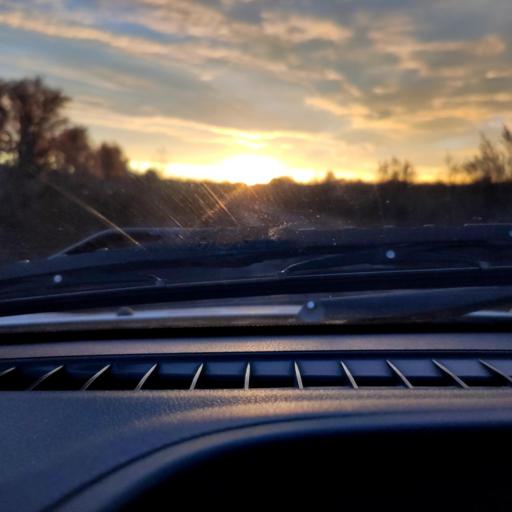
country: RU
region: Samara
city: Tol'yatti
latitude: 53.5955
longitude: 49.4820
